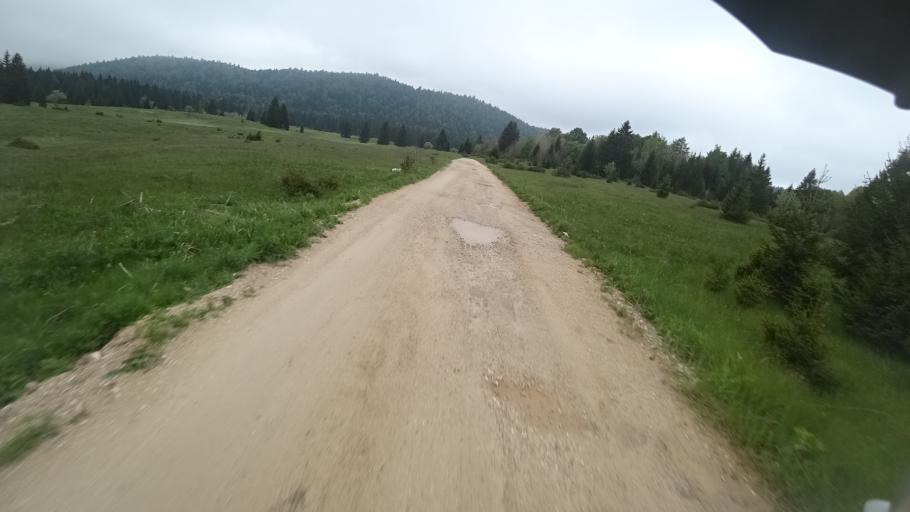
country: BA
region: Federation of Bosnia and Herzegovina
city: Bihac
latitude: 44.6446
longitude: 15.8515
